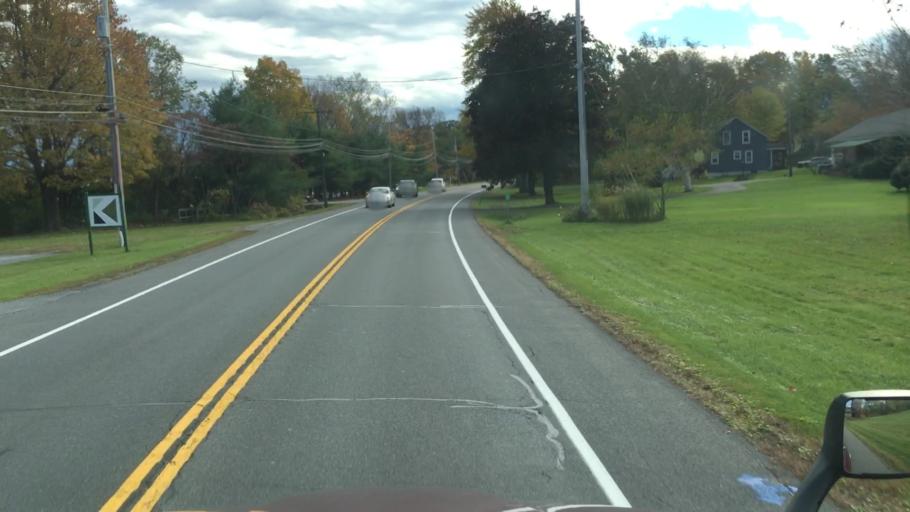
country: US
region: New York
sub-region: Saratoga County
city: Ballston Spa
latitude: 42.9640
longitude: -73.8633
